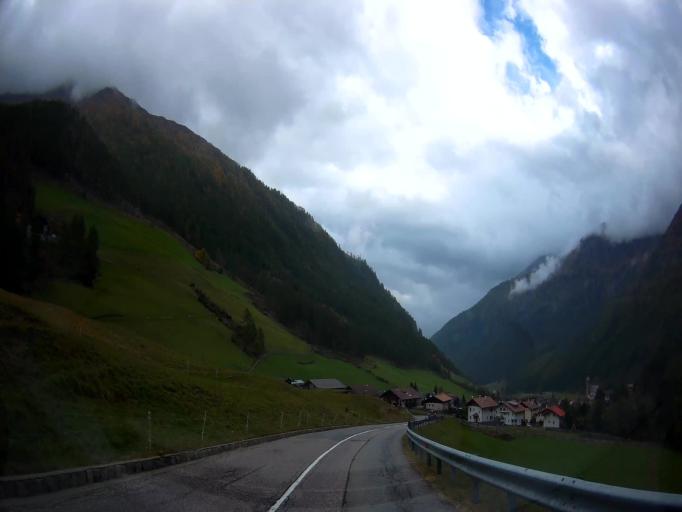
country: IT
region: Trentino-Alto Adige
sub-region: Bolzano
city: Senales
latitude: 46.7280
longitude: 10.8544
